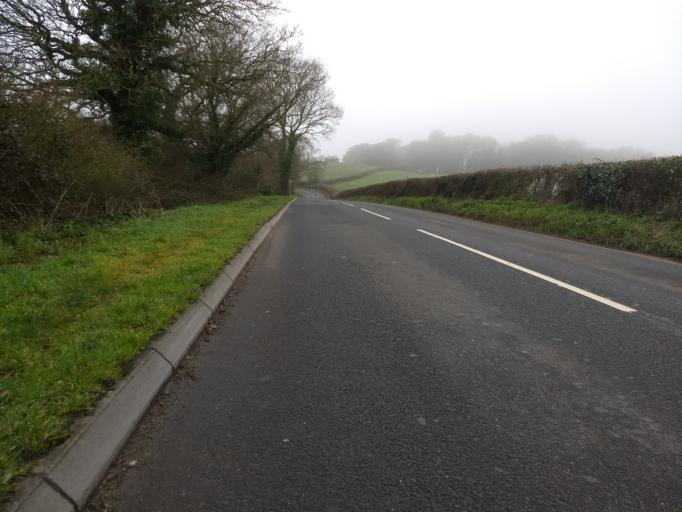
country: GB
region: England
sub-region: Isle of Wight
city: Ryde
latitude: 50.7143
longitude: -1.1977
